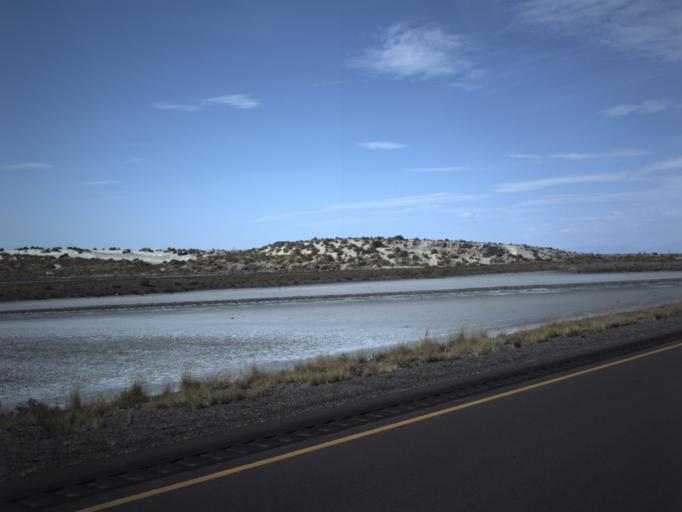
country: US
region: Utah
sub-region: Tooele County
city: Wendover
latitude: 40.7276
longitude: -113.2763
